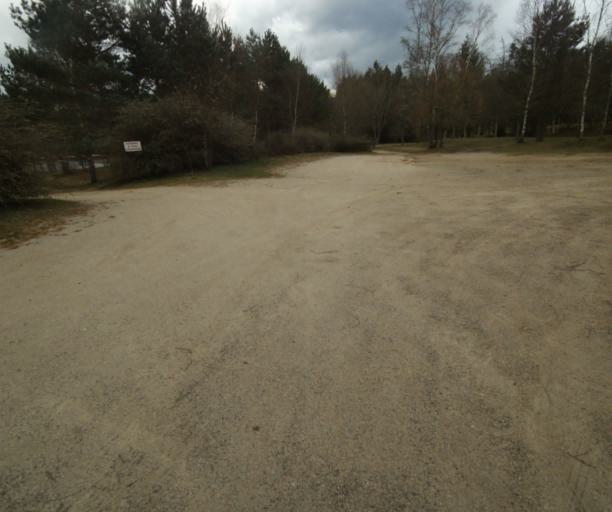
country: FR
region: Limousin
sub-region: Departement de la Correze
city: Correze
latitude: 45.2869
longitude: 1.9752
